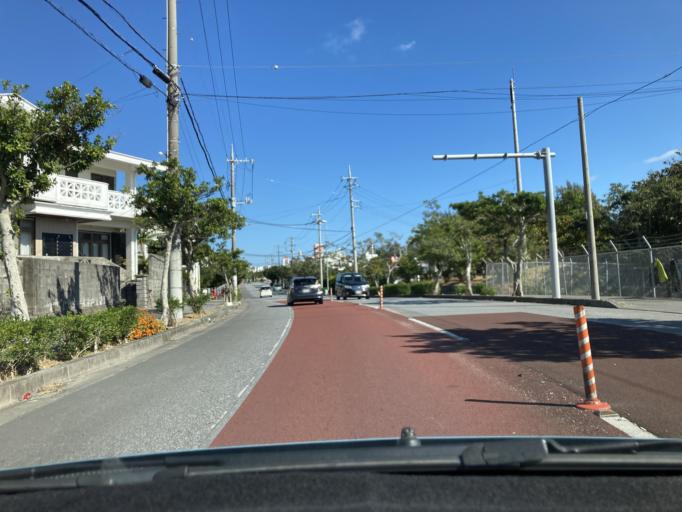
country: JP
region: Okinawa
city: Gushikawa
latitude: 26.3521
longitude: 127.8434
